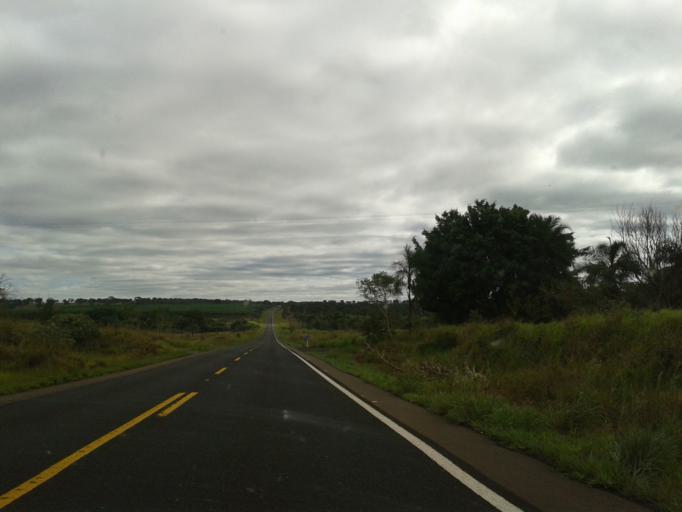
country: BR
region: Minas Gerais
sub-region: Campina Verde
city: Campina Verde
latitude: -19.5153
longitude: -49.6567
